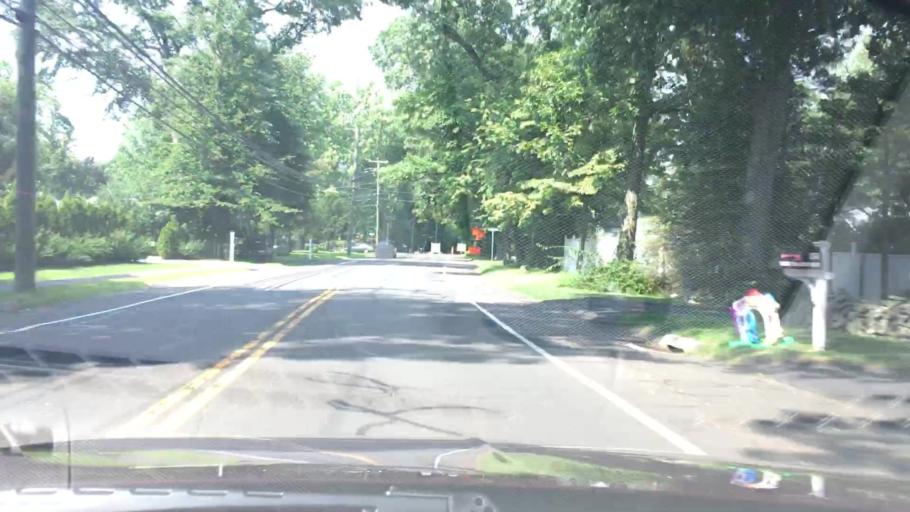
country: US
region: Connecticut
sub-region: Fairfield County
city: Norwalk
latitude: 41.1408
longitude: -73.4175
